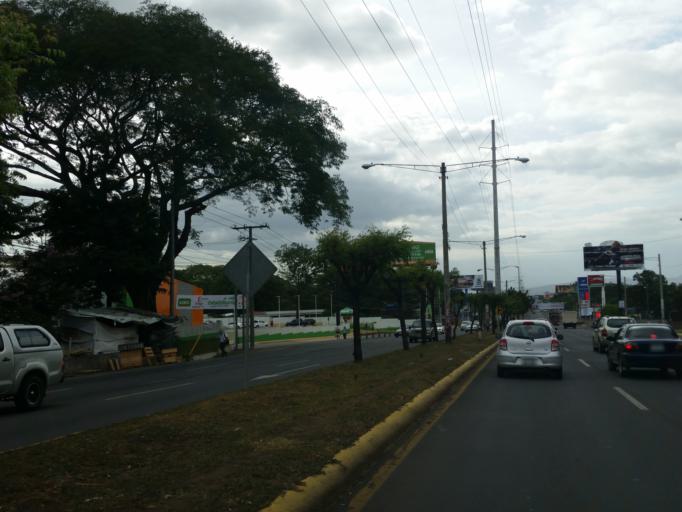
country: NI
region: Managua
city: Managua
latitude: 12.0960
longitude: -86.2395
